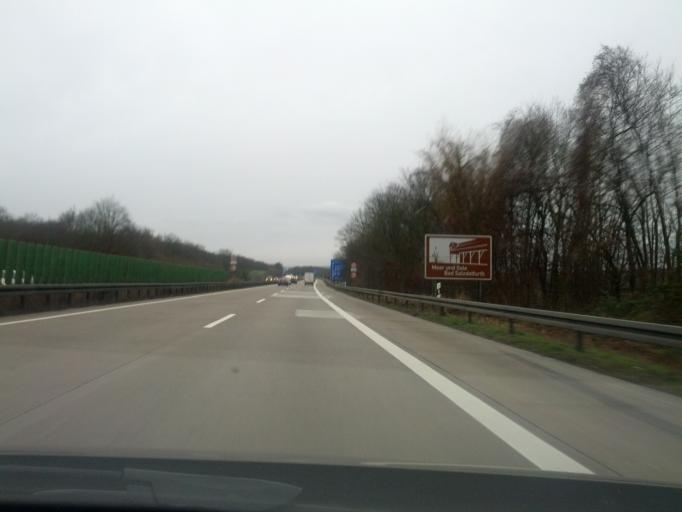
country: DE
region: Lower Saxony
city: Holle
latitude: 52.1136
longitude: 10.1296
